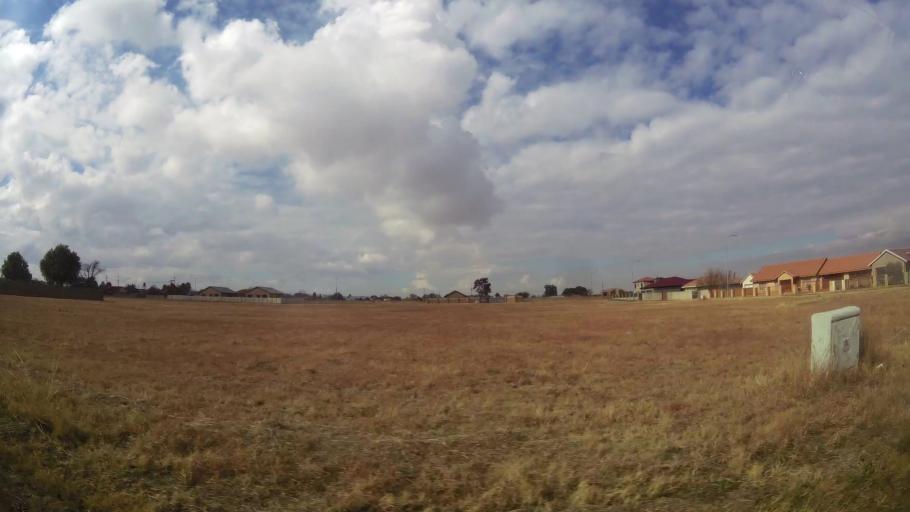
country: ZA
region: Gauteng
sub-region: Sedibeng District Municipality
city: Meyerton
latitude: -26.6101
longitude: 28.0489
